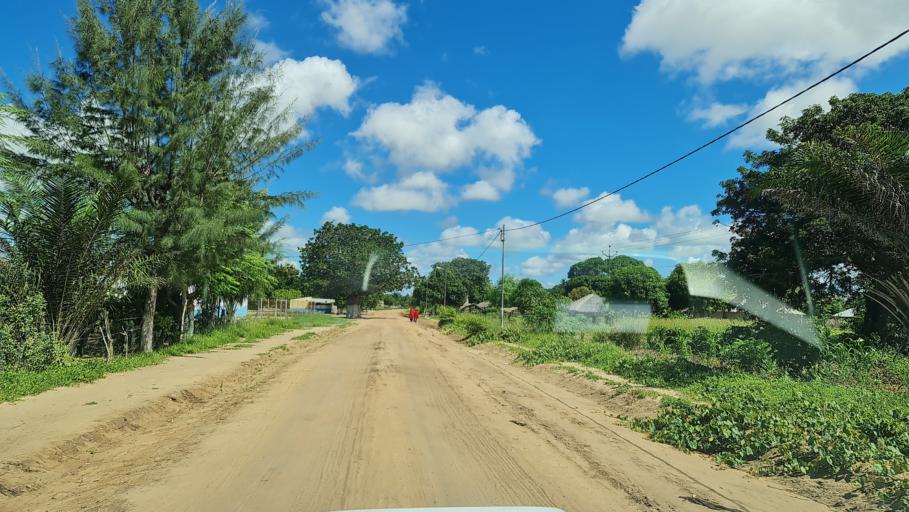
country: MZ
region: Nampula
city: Ilha de Mocambique
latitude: -15.5565
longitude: 40.4119
